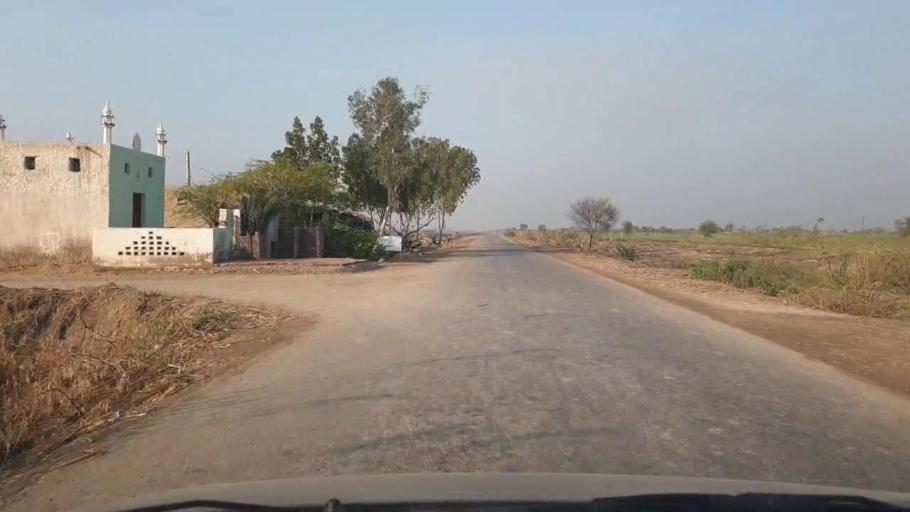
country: PK
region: Sindh
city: Mirwah Gorchani
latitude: 25.3481
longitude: 69.1718
